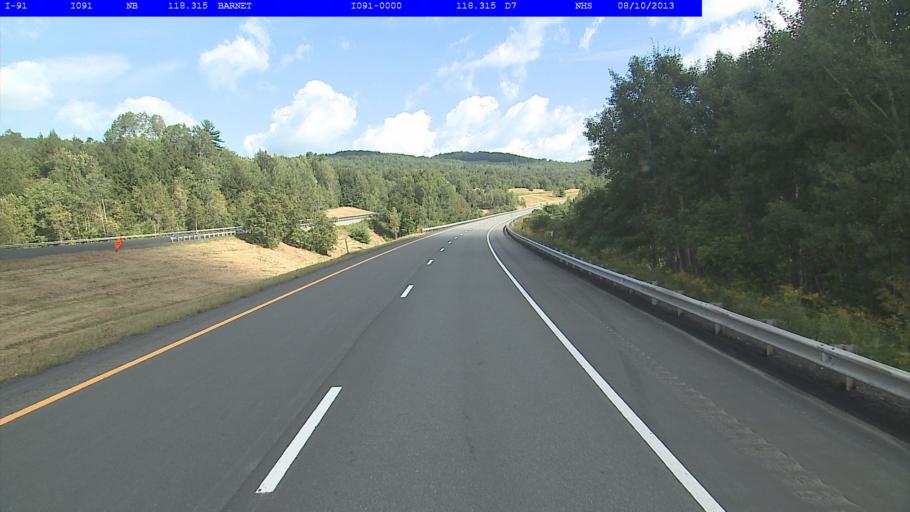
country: US
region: New Hampshire
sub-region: Grafton County
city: Woodsville
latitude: 44.2701
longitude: -72.0714
